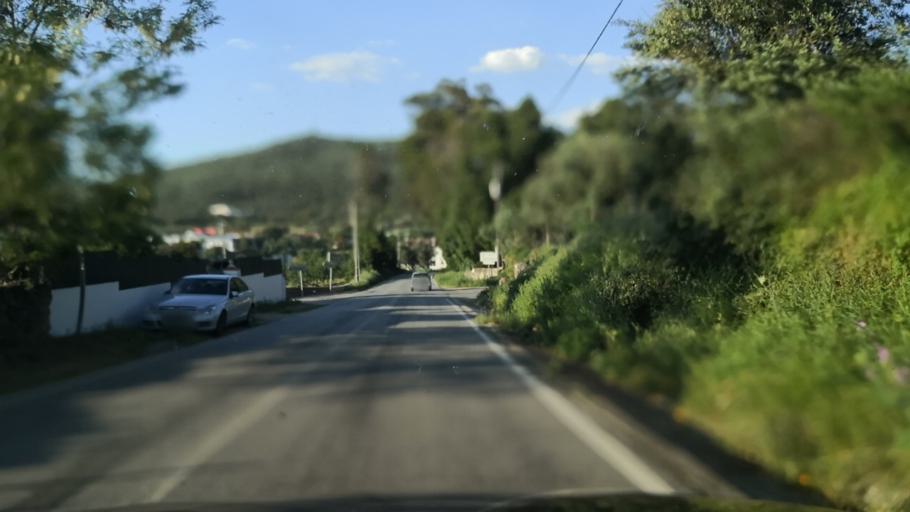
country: PT
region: Portalegre
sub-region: Portalegre
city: Portalegre
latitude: 39.3237
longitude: -7.4364
